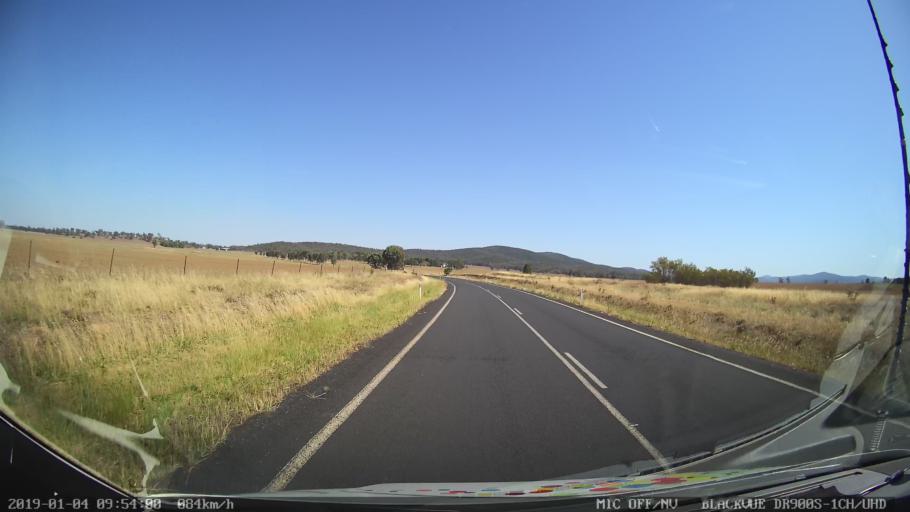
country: AU
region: New South Wales
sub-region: Cabonne
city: Canowindra
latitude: -33.5456
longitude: 148.4187
